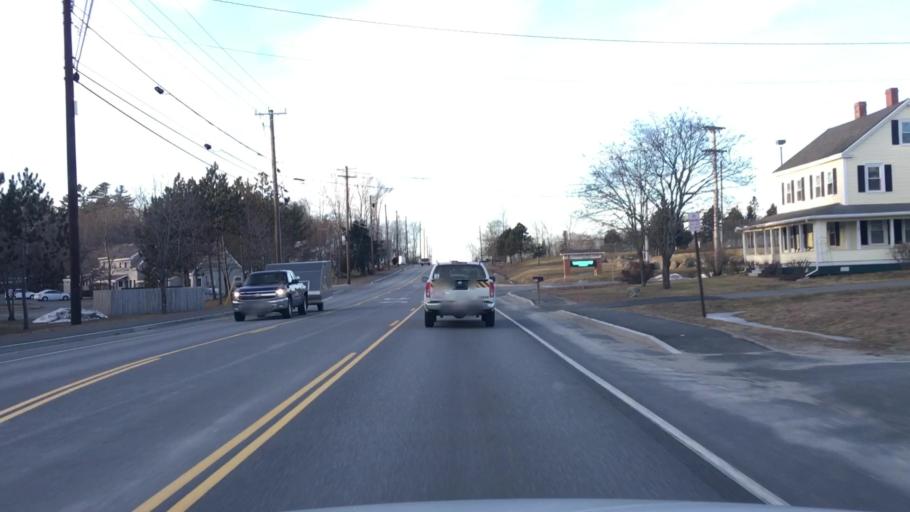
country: US
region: Maine
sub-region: Hancock County
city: Ellsworth
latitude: 44.5536
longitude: -68.4302
